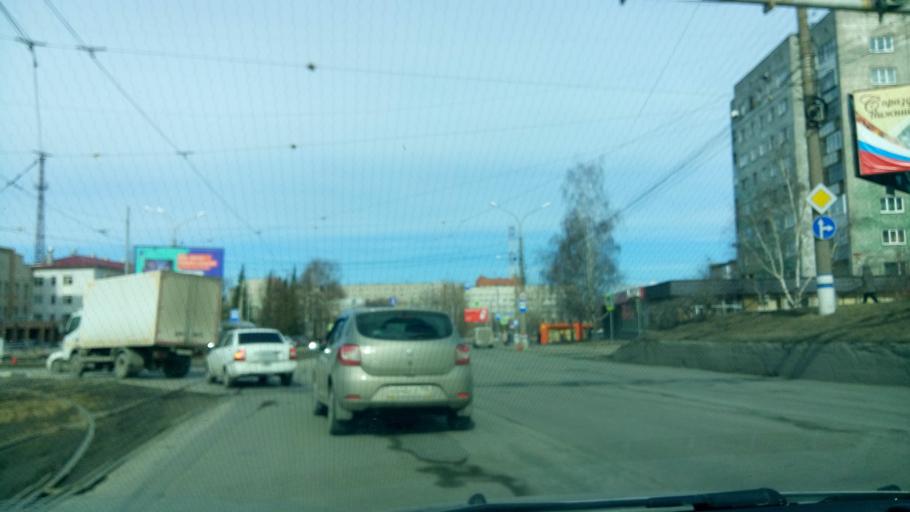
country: RU
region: Sverdlovsk
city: Nizhniy Tagil
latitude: 57.9085
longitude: 59.9474
